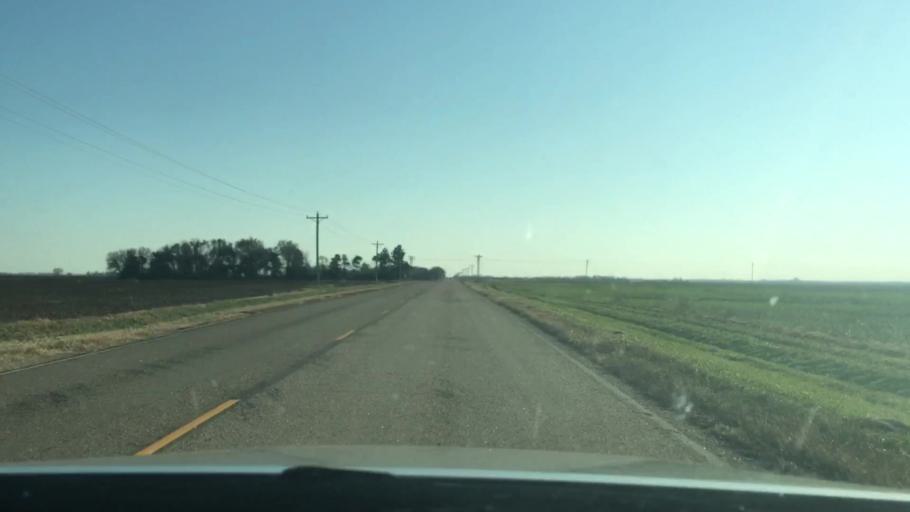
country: US
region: Kansas
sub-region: Reno County
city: Nickerson
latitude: 38.2056
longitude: -98.0877
